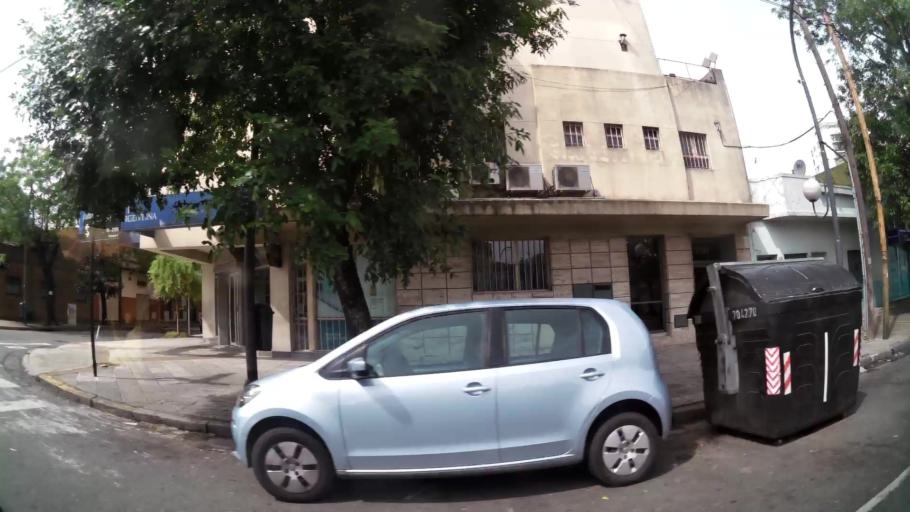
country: AR
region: Buenos Aires
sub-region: Partido de Avellaneda
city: Avellaneda
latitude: -34.6514
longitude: -58.4192
